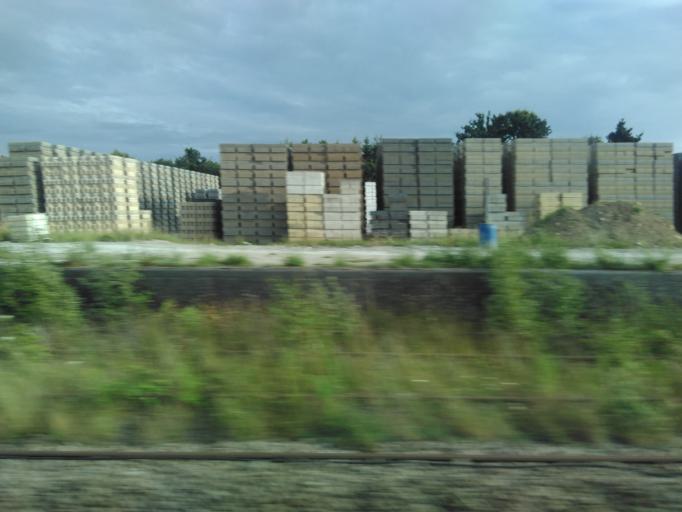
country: GB
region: England
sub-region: Norfolk
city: Weeting
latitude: 52.4540
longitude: 0.6263
